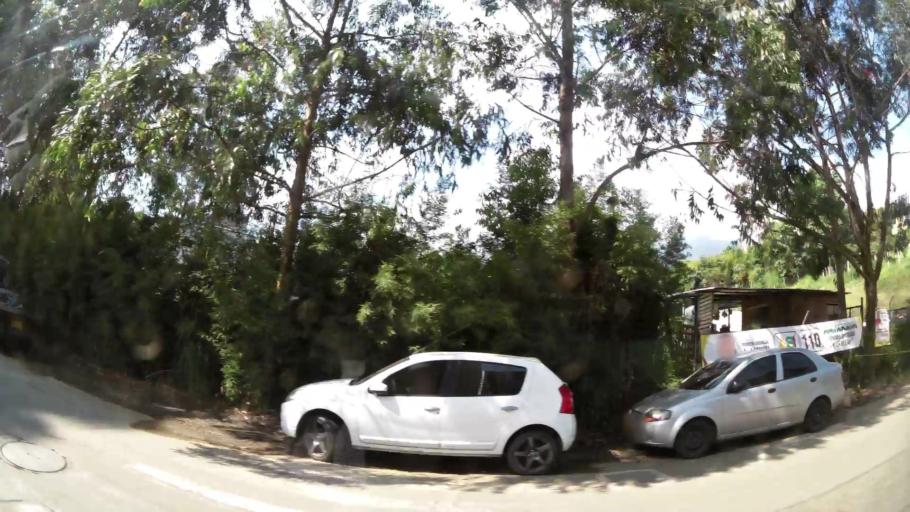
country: CO
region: Antioquia
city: La Estrella
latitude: 6.1678
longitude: -75.6489
